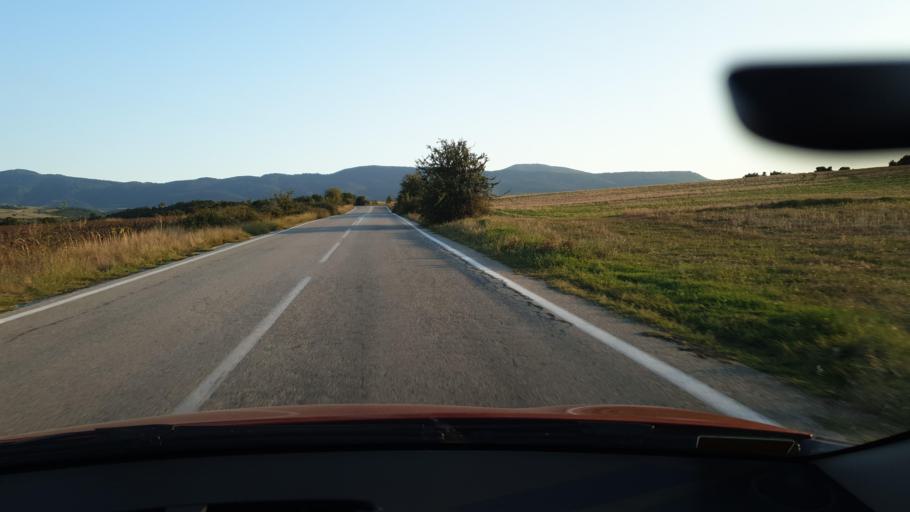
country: GR
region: Central Macedonia
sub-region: Nomos Thessalonikis
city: Nea Apollonia
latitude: 40.5410
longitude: 23.4694
